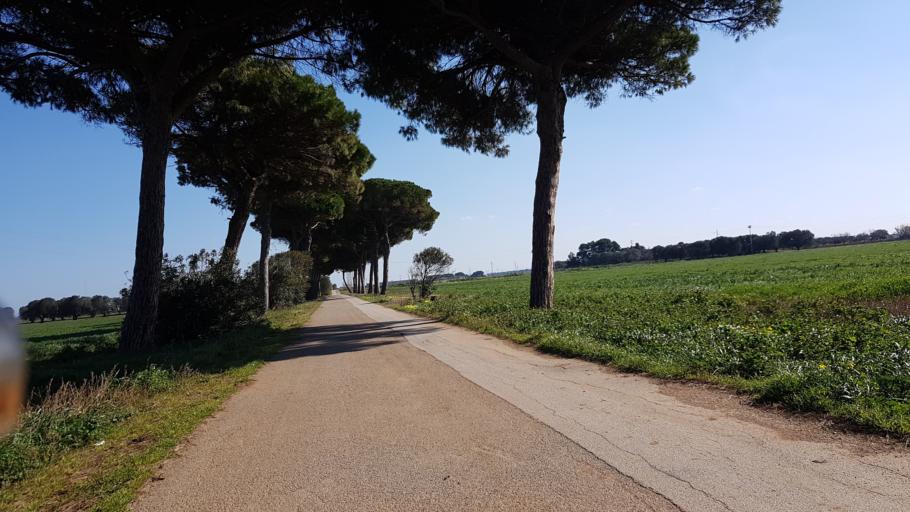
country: IT
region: Apulia
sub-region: Provincia di Brindisi
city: Mesagne
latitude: 40.6198
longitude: 17.8530
